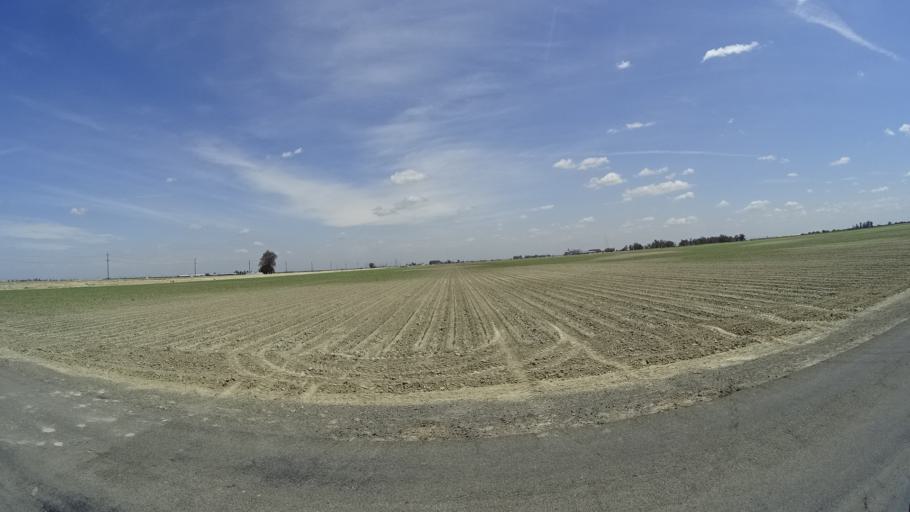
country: US
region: California
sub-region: Kings County
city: Home Garden
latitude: 36.2242
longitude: -119.6729
